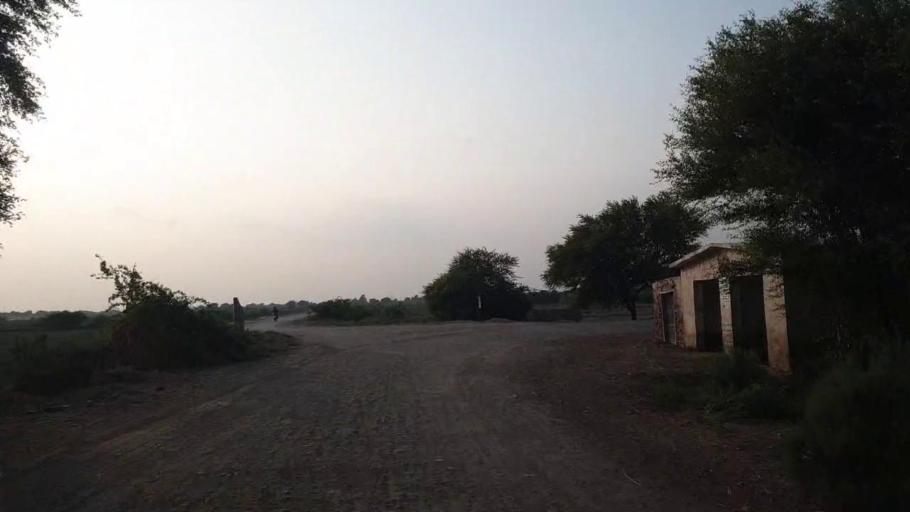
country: PK
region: Sindh
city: Tando Ghulam Ali
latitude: 25.0671
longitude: 68.9599
